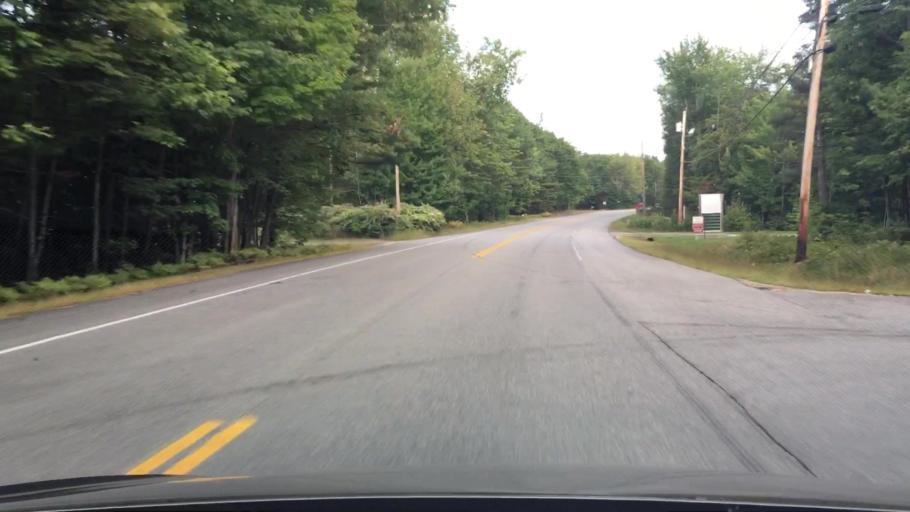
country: US
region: Maine
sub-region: Cumberland County
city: Bridgton
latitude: 44.0661
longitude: -70.7526
